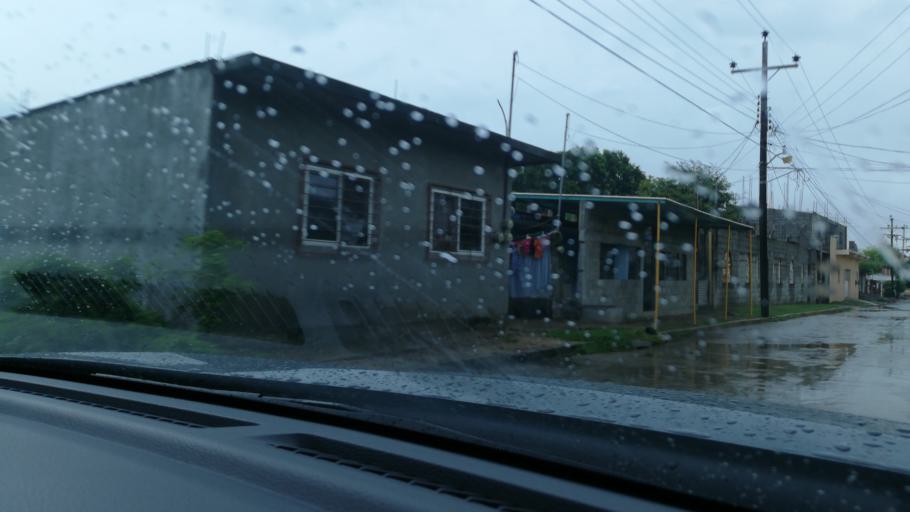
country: MX
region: Oaxaca
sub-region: Salina Cruz
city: Salina Cruz
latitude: 16.2054
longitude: -95.1953
